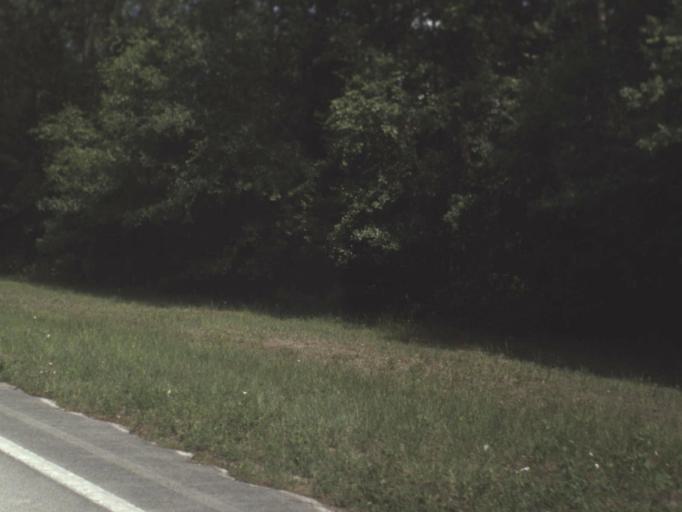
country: US
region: Florida
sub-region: Bradford County
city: Starke
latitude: 29.9385
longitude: -82.0402
